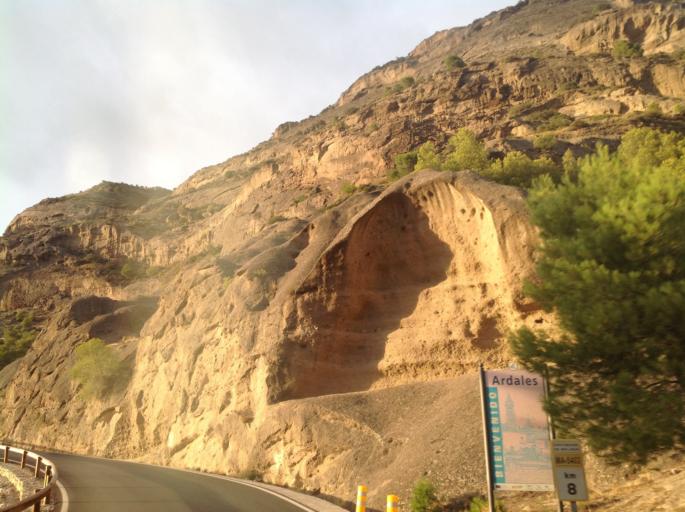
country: ES
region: Andalusia
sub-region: Provincia de Malaga
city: Carratraca
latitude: 36.9124
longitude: -4.7868
